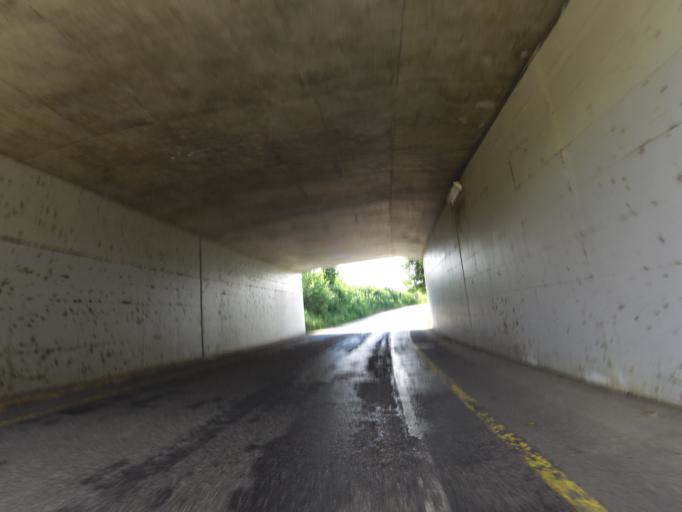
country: CH
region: Aargau
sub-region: Bezirk Aarau
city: Graenichen
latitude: 47.3824
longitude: 8.1115
